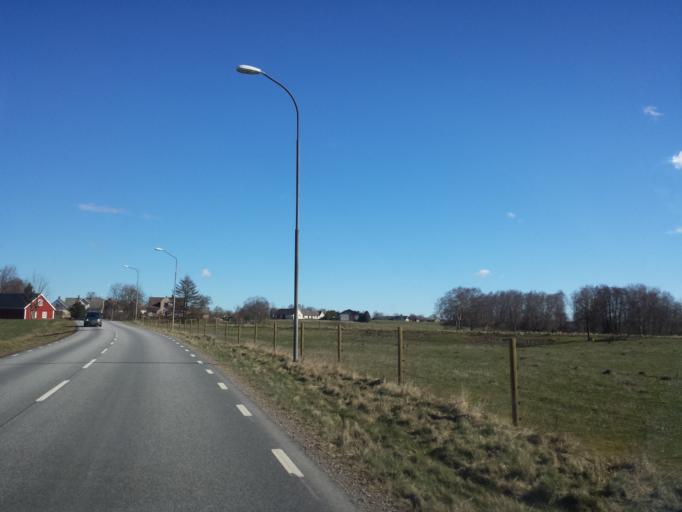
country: SE
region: Skane
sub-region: Tomelilla Kommun
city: Tomelilla
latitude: 55.6489
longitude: 13.8937
